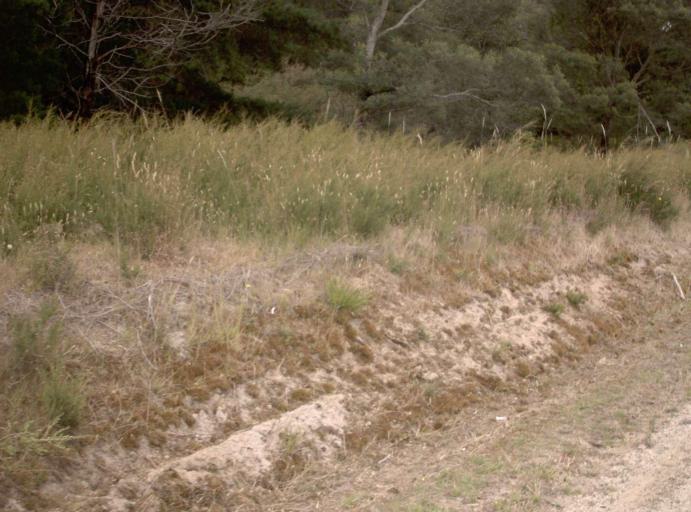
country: AU
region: Victoria
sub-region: Wellington
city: Sale
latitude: -38.1705
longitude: 147.0331
